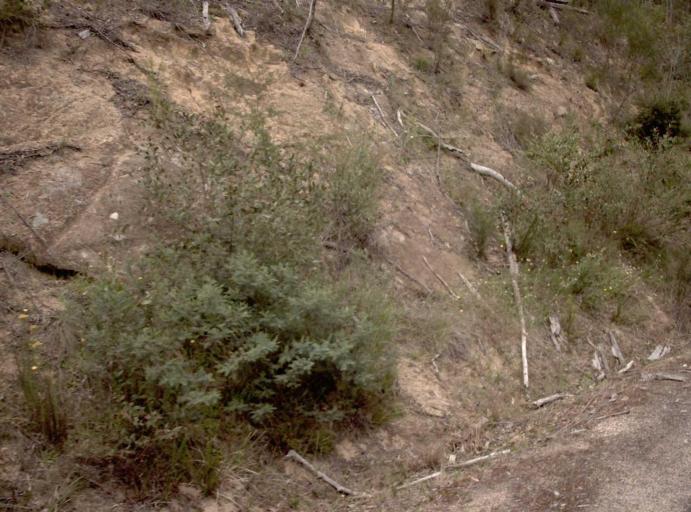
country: AU
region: New South Wales
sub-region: Bombala
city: Bombala
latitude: -37.3472
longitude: 149.2025
